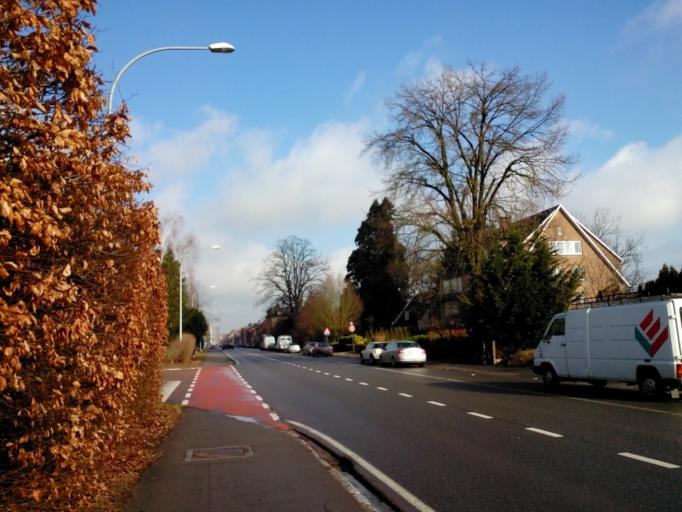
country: BE
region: Flanders
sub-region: Provincie Vlaams-Brabant
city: Leuven
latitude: 50.8536
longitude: 4.6956
